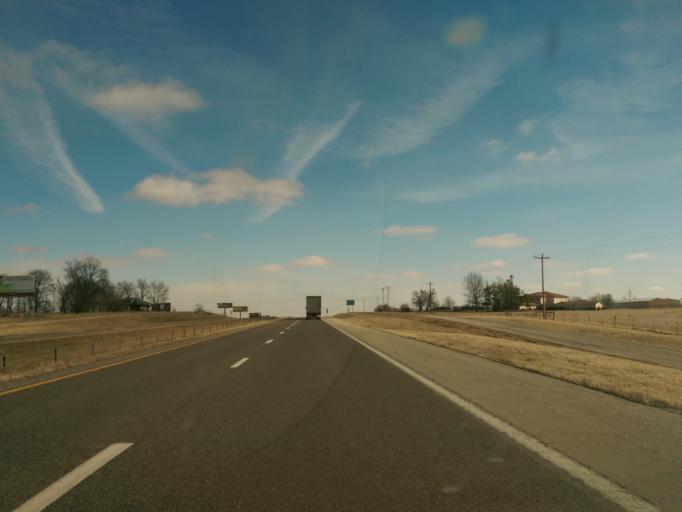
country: US
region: Missouri
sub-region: Callaway County
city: Fulton
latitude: 38.9438
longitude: -91.9041
